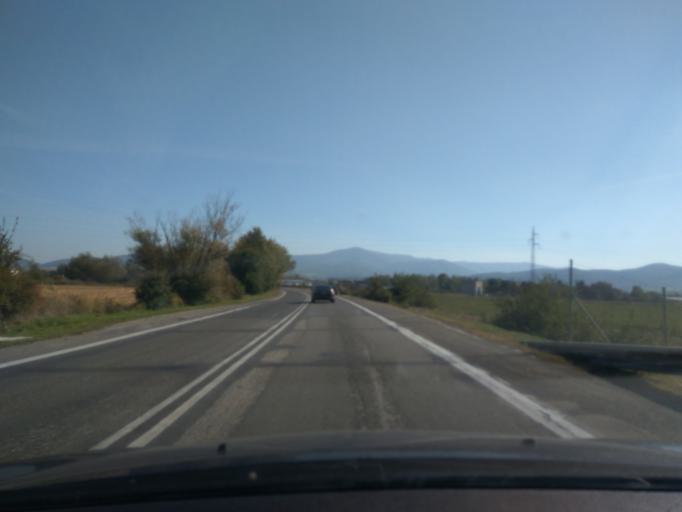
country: SK
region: Trenciansky
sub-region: Okres Trencin
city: Trencin
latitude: 48.8572
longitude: 17.9599
